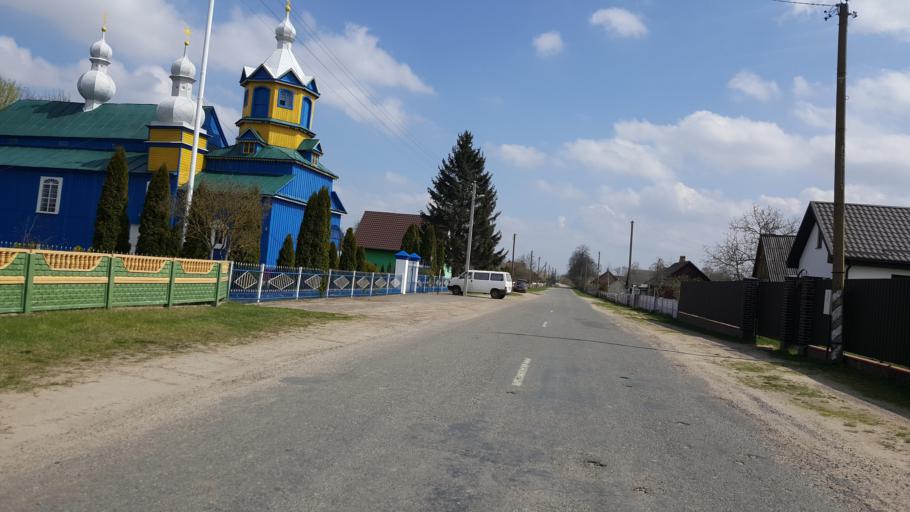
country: BY
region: Brest
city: Zhabinka
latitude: 52.2700
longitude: 23.9935
